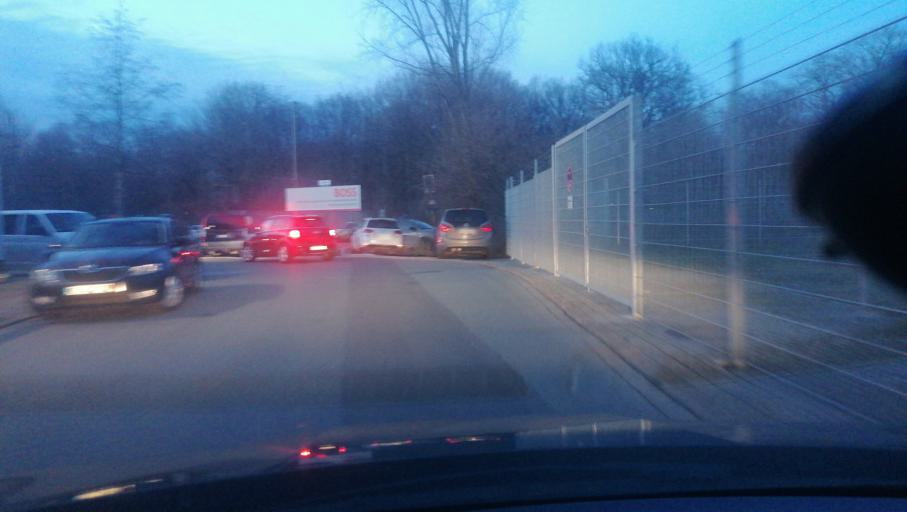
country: DE
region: North Rhine-Westphalia
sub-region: Regierungsbezirk Arnsberg
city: Dortmund
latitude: 51.5354
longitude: 7.4386
